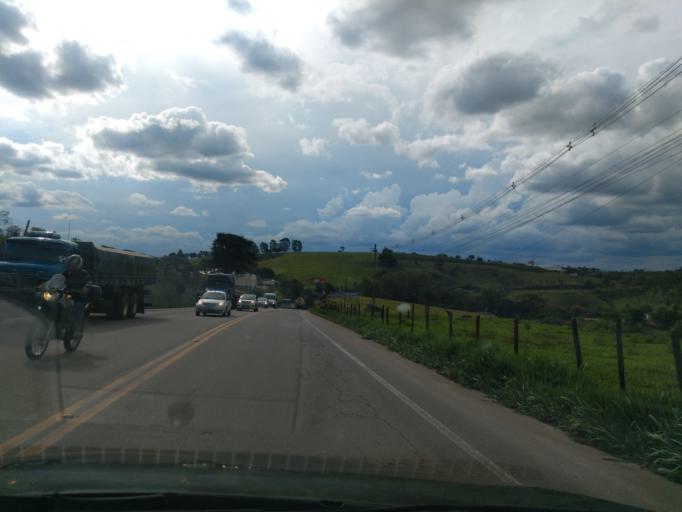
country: BR
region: Minas Gerais
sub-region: Varginha
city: Varginha
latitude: -21.6139
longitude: -45.4248
